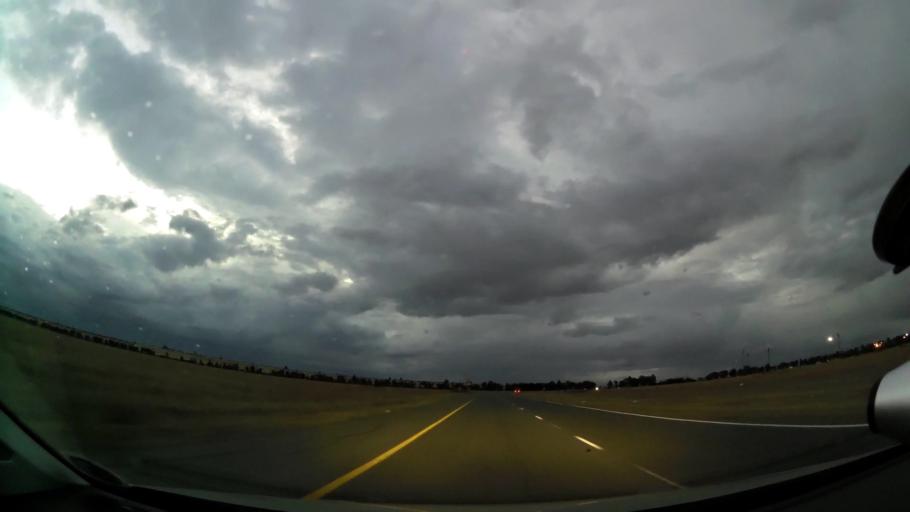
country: ZA
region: Orange Free State
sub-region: Lejweleputswa District Municipality
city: Welkom
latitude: -27.9439
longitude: 26.7917
